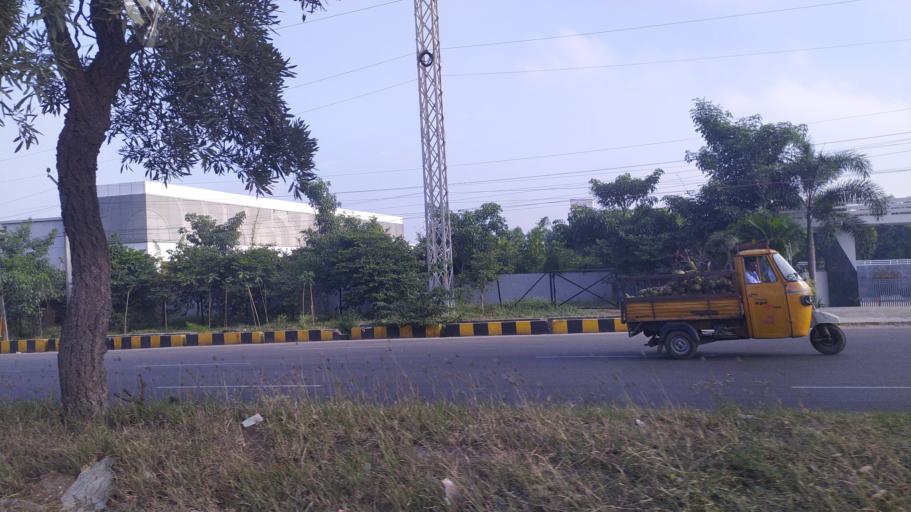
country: IN
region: Telangana
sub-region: Rangareddi
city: Balapur
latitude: 17.3174
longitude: 78.4386
